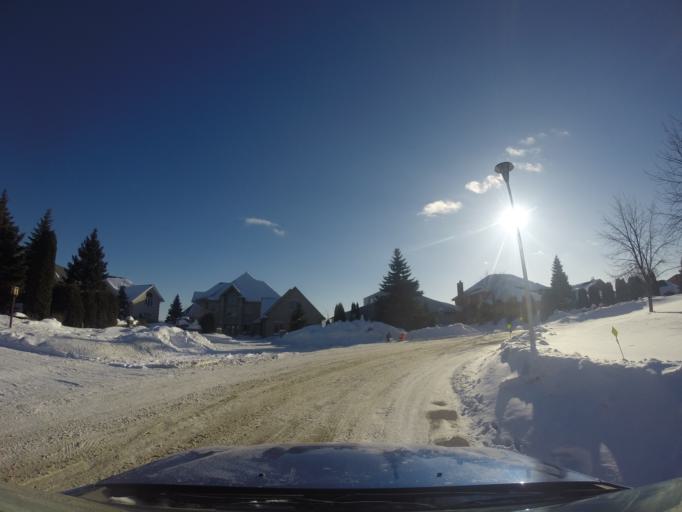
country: CA
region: Ontario
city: Greater Sudbury
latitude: 46.4575
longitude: -80.9888
